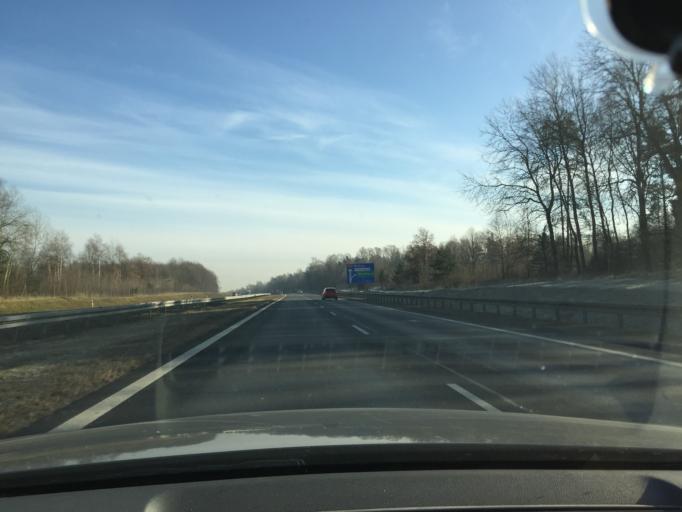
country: PL
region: Silesian Voivodeship
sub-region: Katowice
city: Murcki
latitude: 50.2219
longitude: 19.0954
